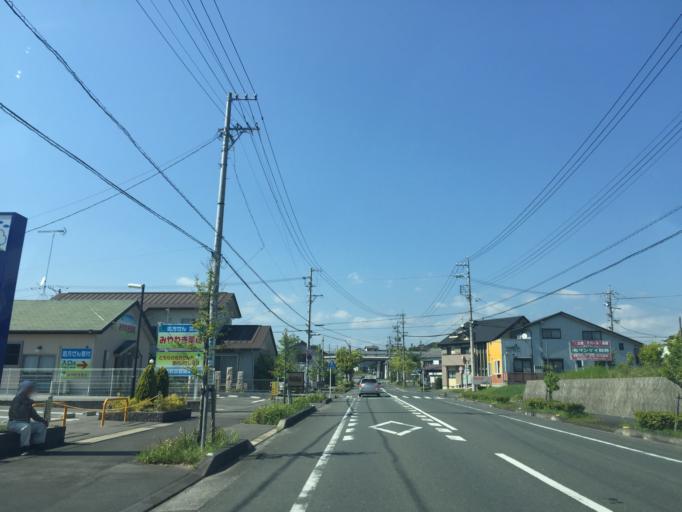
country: JP
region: Shizuoka
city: Kakegawa
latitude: 34.7824
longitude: 138.0282
